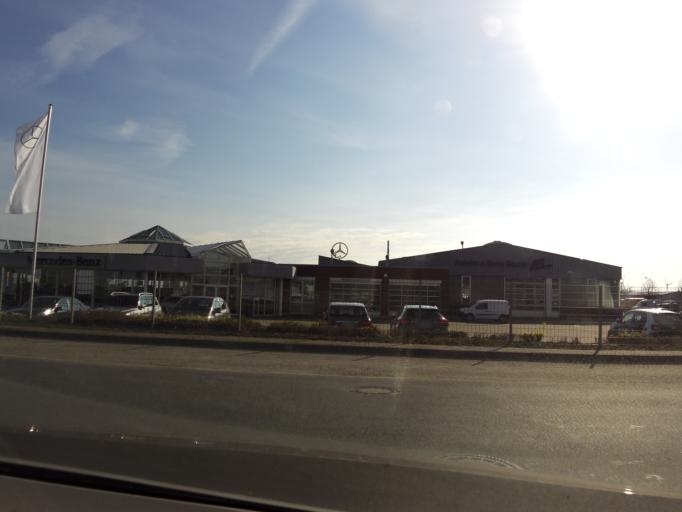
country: DE
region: Mecklenburg-Vorpommern
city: Ribnitz-Damgarten
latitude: 54.2544
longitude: 12.4919
